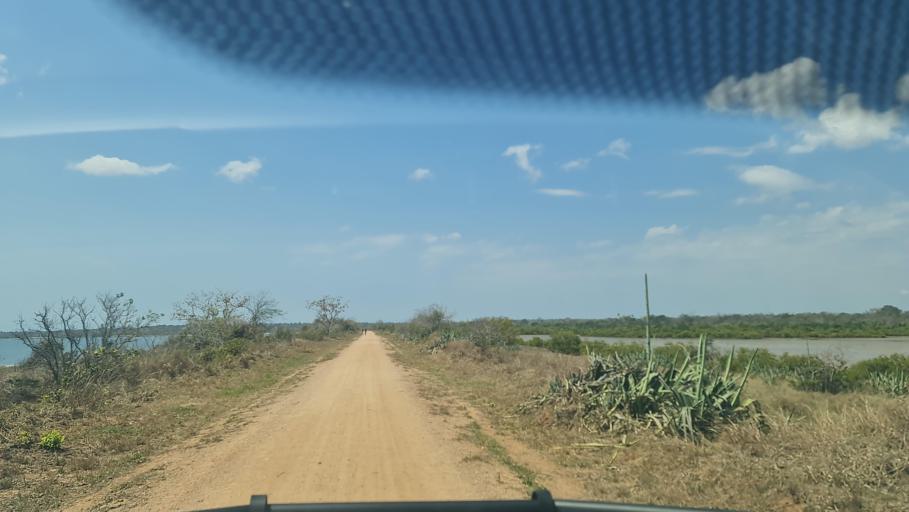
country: MZ
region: Nampula
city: Ilha de Mocambique
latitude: -15.1802
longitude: 40.5151
